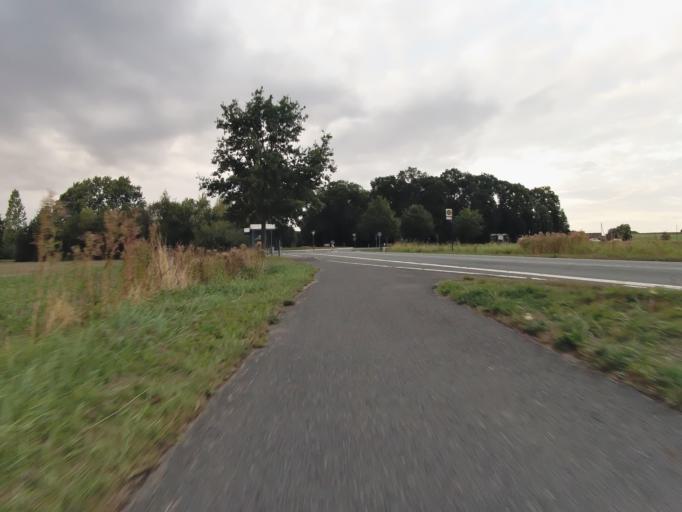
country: DE
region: North Rhine-Westphalia
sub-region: Regierungsbezirk Munster
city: Westerkappeln
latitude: 52.2785
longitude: 7.8638
